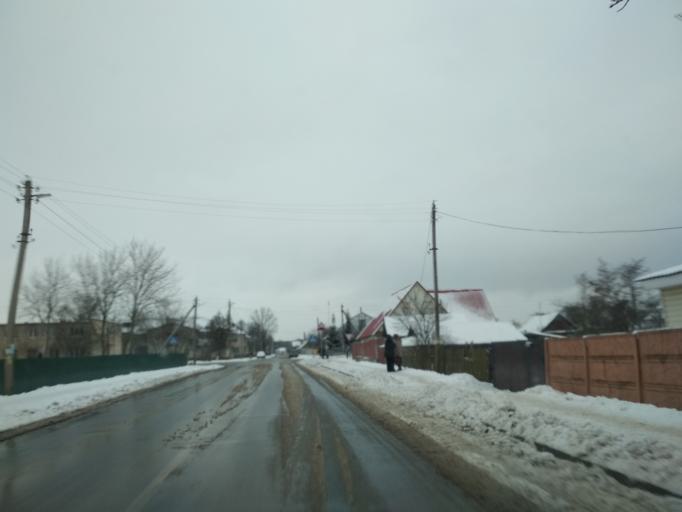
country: BY
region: Minsk
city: Mar''ina Horka
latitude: 53.5116
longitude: 28.1320
